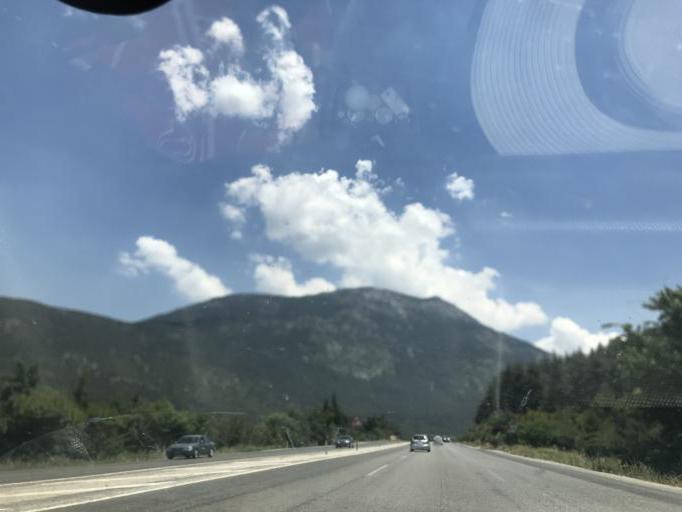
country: TR
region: Denizli
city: Honaz
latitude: 37.7265
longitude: 29.2020
